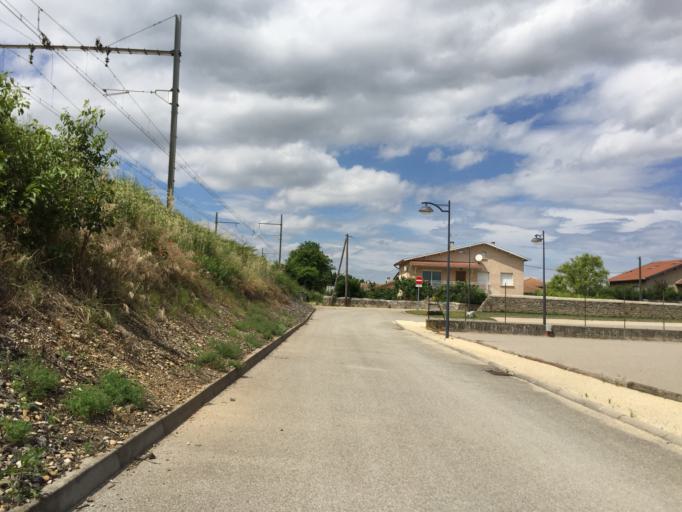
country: FR
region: Rhone-Alpes
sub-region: Departement de la Drome
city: Andancette
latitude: 45.2708
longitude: 4.7987
